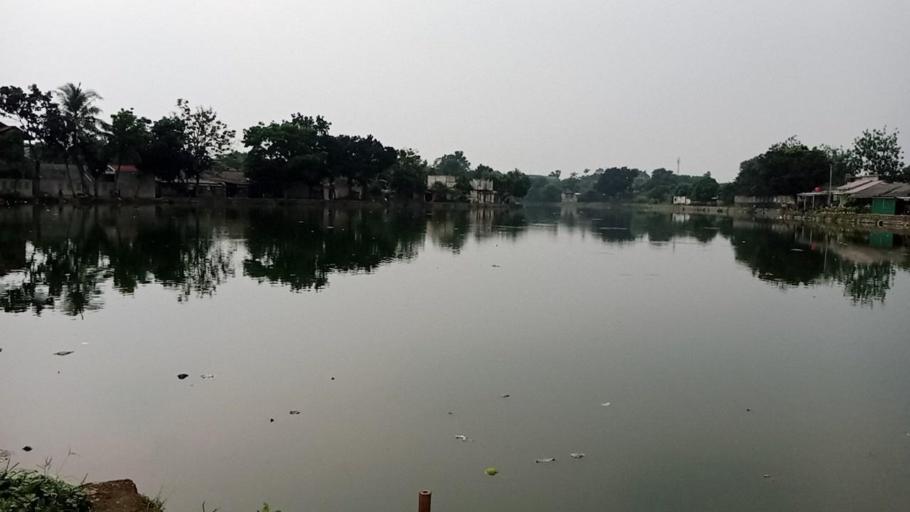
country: ID
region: West Java
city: Depok
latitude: -6.4434
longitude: 106.8000
